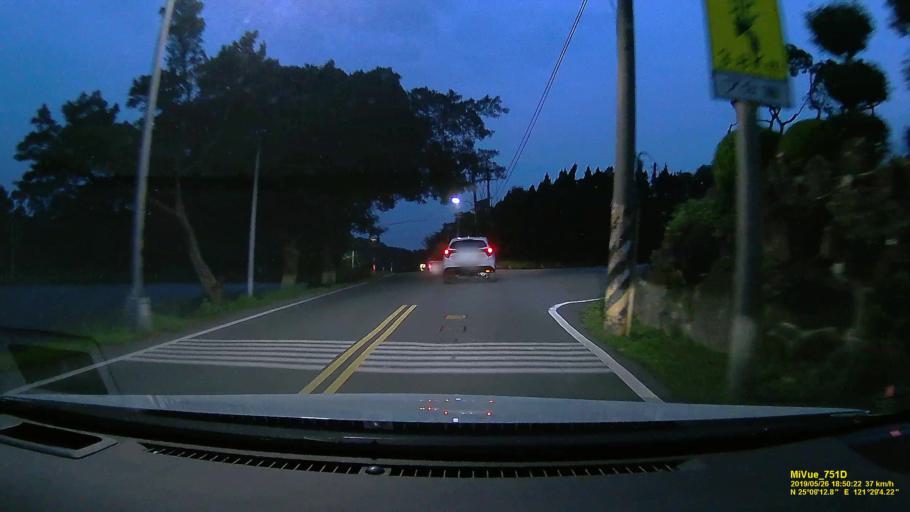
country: TW
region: Taipei
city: Taipei
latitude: 25.1534
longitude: 121.4844
